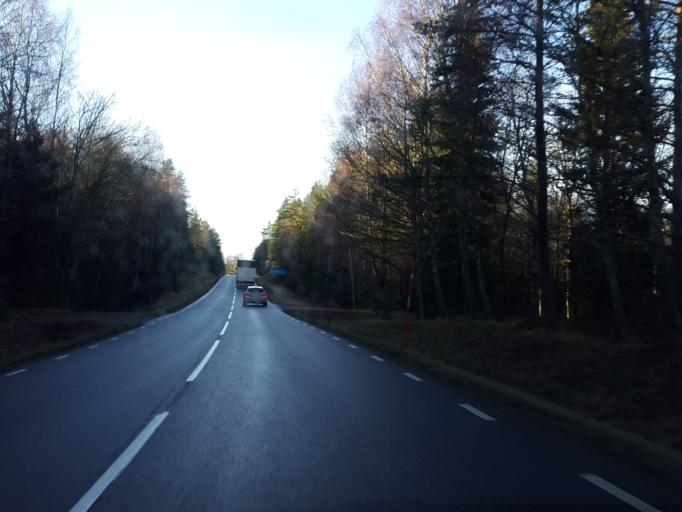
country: SE
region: Vaestra Goetaland
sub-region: Vargarda Kommun
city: Vargarda
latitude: 57.9907
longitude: 12.8204
